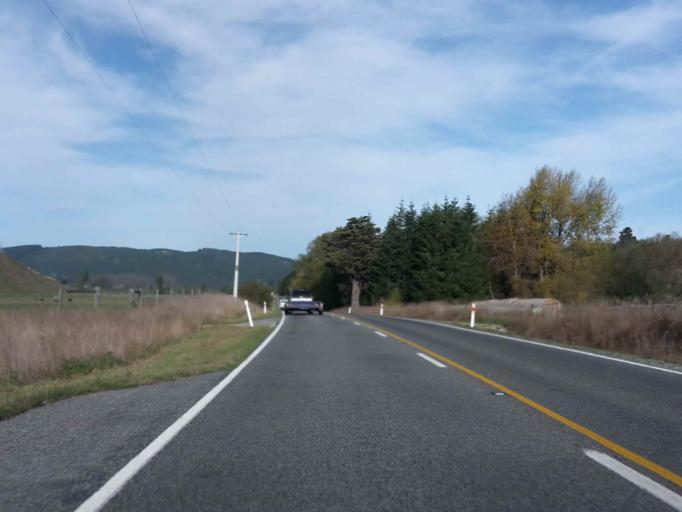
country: NZ
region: Canterbury
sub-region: Timaru District
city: Pleasant Point
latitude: -44.1087
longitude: 171.0100
